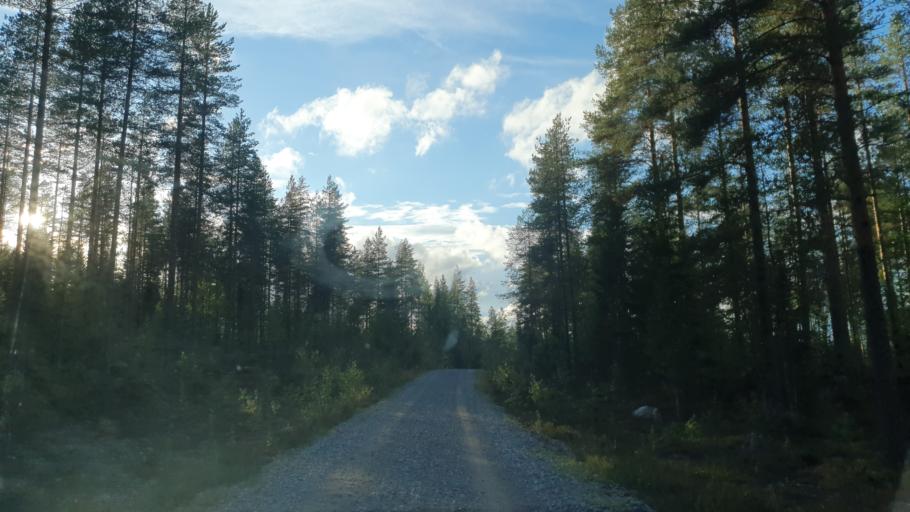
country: FI
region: Kainuu
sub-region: Kehys-Kainuu
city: Kuhmo
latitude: 64.3396
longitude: 29.9808
